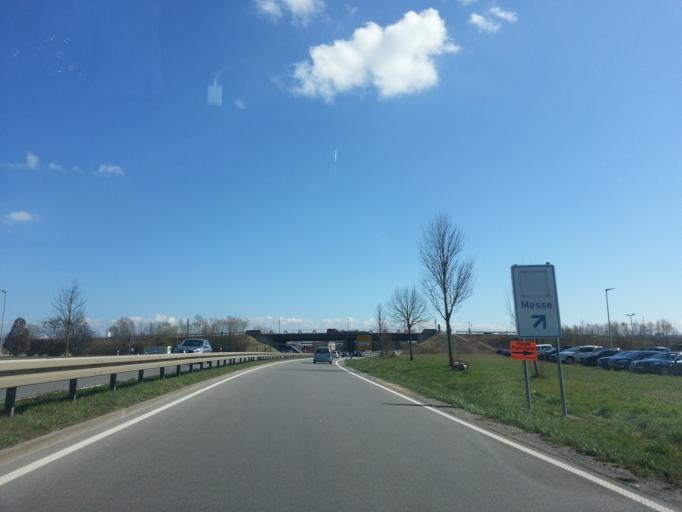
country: DE
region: Baden-Wuerttemberg
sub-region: Tuebingen Region
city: Friedrichshafen
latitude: 47.6660
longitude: 9.4912
